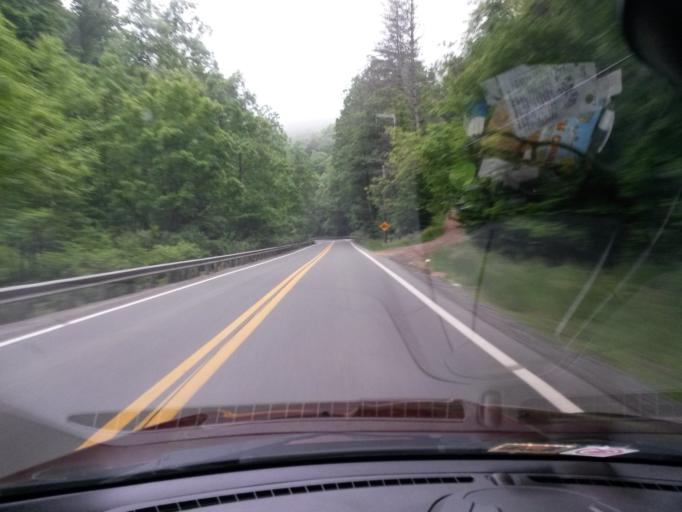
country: US
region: West Virginia
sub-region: Wyoming County
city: Pineville
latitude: 37.5616
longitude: -81.5372
